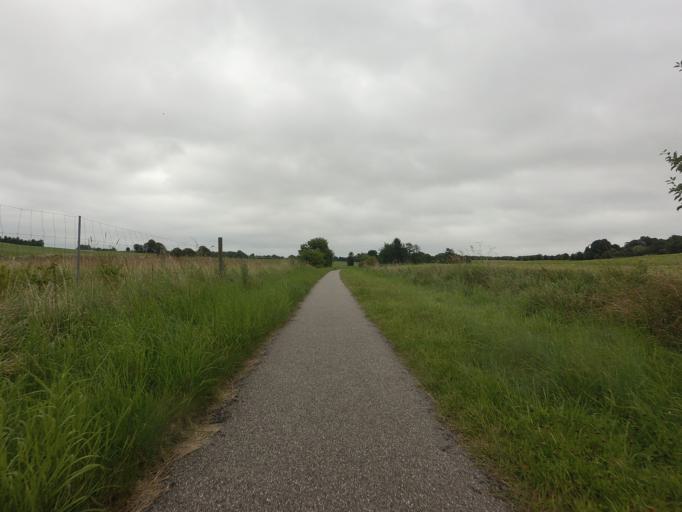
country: DK
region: Central Jutland
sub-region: Horsens Kommune
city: Braedstrup
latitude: 56.0254
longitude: 9.5532
